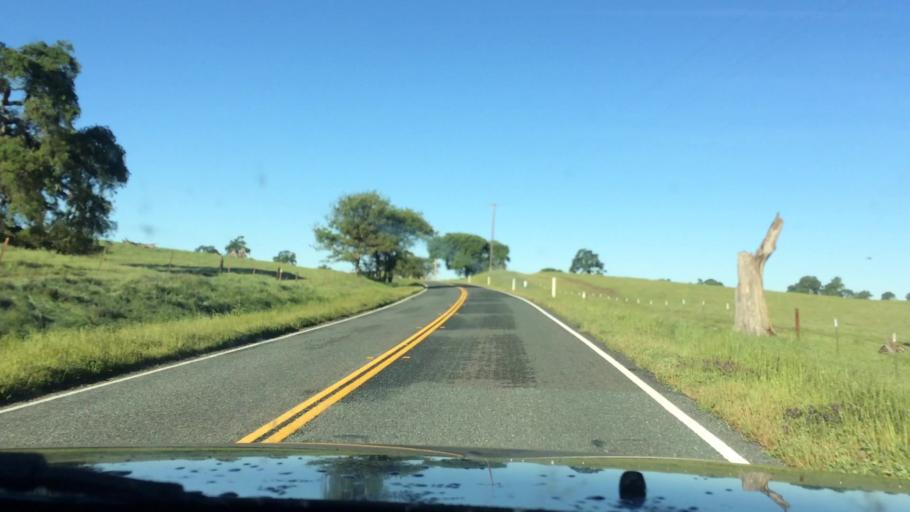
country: US
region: California
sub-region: Amador County
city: Ione
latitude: 38.3858
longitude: -121.0488
